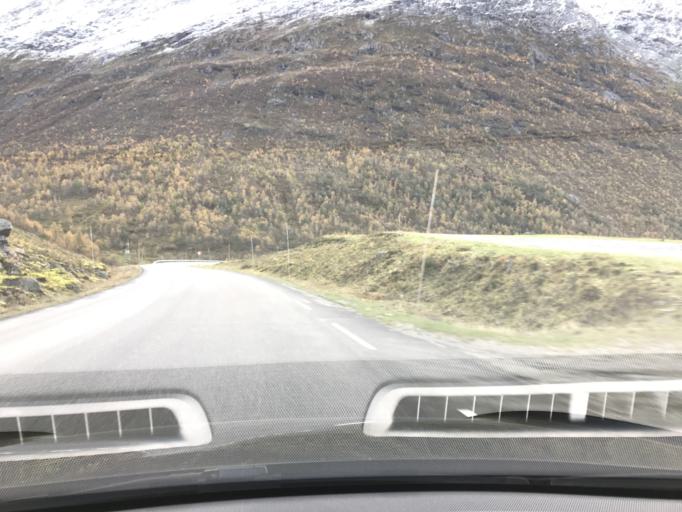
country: NO
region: More og Romsdal
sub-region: Norddal
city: Valldal
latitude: 61.9673
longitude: 7.2502
